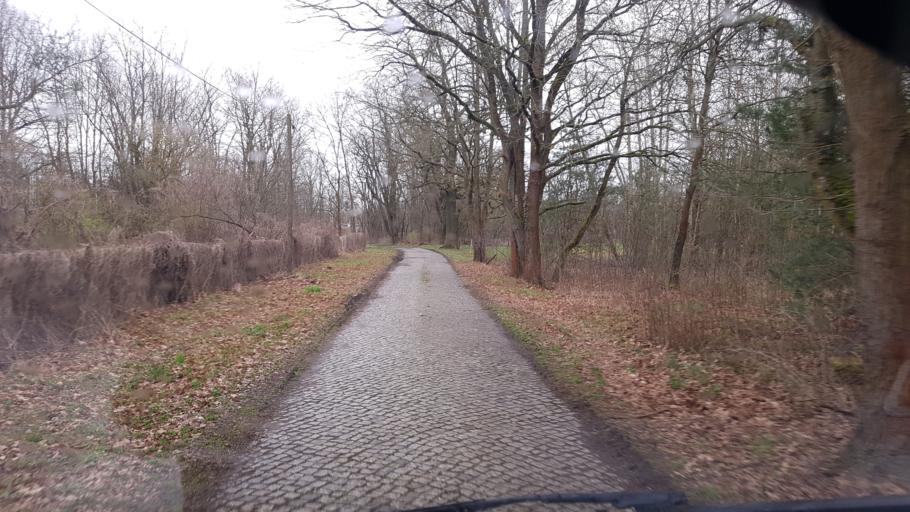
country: DE
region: Brandenburg
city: Ruhland
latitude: 51.4469
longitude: 13.8603
